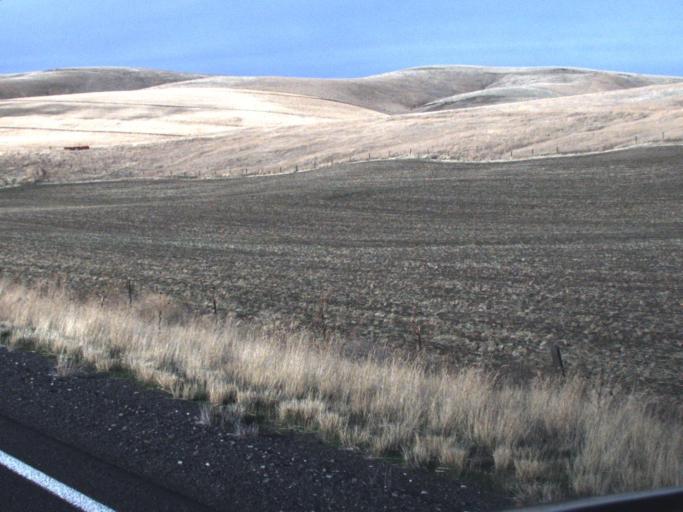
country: US
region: Washington
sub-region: Garfield County
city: Pomeroy
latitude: 46.4817
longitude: -117.7372
